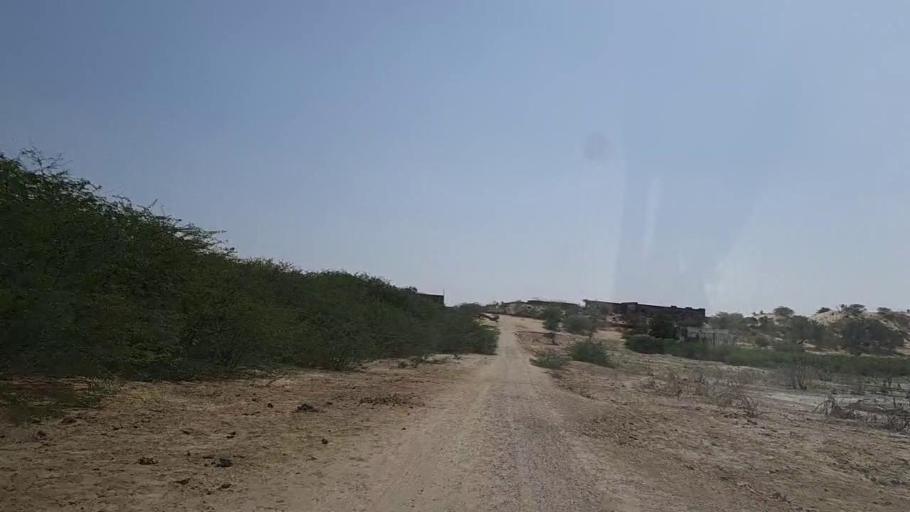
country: PK
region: Sindh
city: Diplo
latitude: 24.5118
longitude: 69.4139
